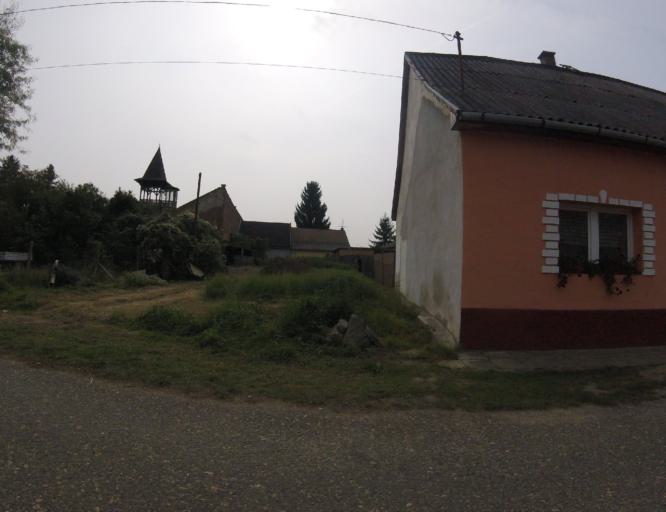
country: HU
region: Pest
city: Veroce
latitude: 47.8267
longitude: 19.0379
